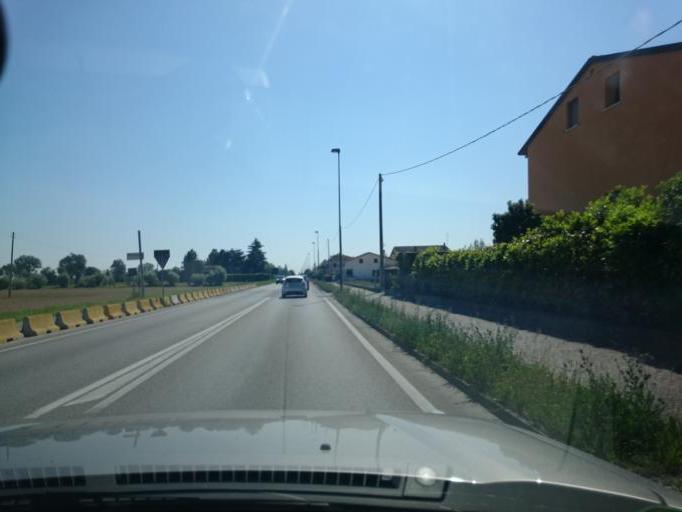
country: IT
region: Veneto
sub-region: Provincia di Venezia
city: Santa Maria di Sala
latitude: 45.5038
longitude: 12.0395
